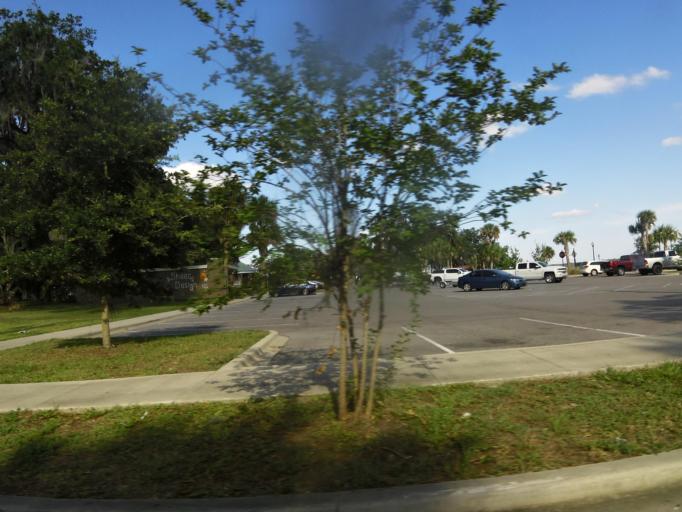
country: US
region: Florida
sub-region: Putnam County
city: Palatka
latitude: 29.6450
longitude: -81.6314
